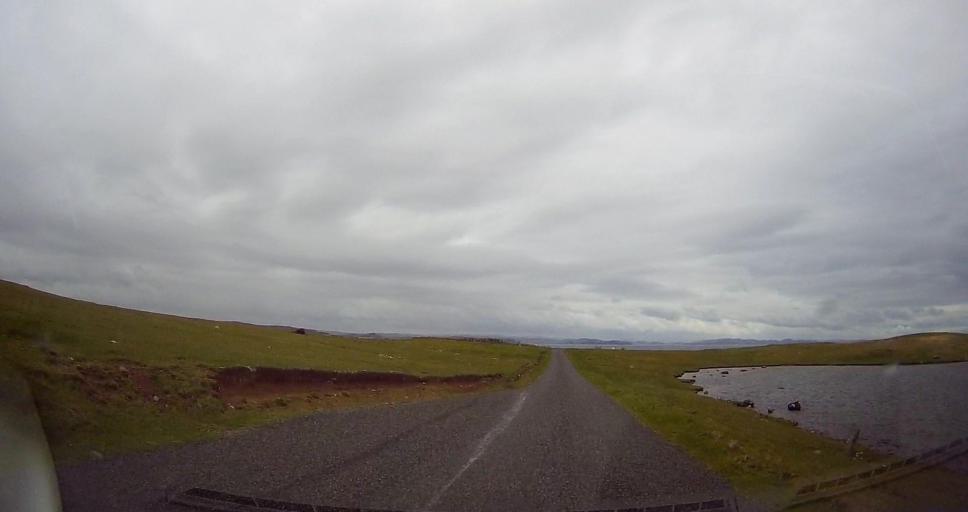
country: GB
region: Scotland
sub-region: Shetland Islands
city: Lerwick
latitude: 60.4894
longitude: -1.6199
